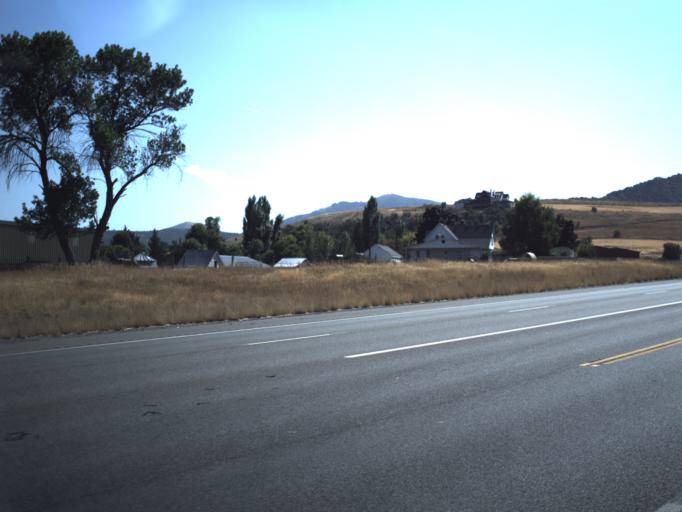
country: US
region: Utah
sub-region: Cache County
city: Wellsville
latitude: 41.6098
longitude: -111.9389
